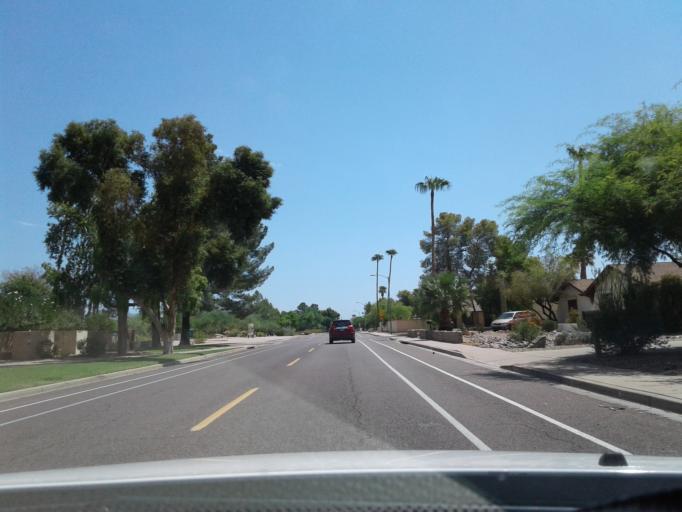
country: US
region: Arizona
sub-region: Maricopa County
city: Paradise Valley
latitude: 33.5900
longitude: -111.9921
